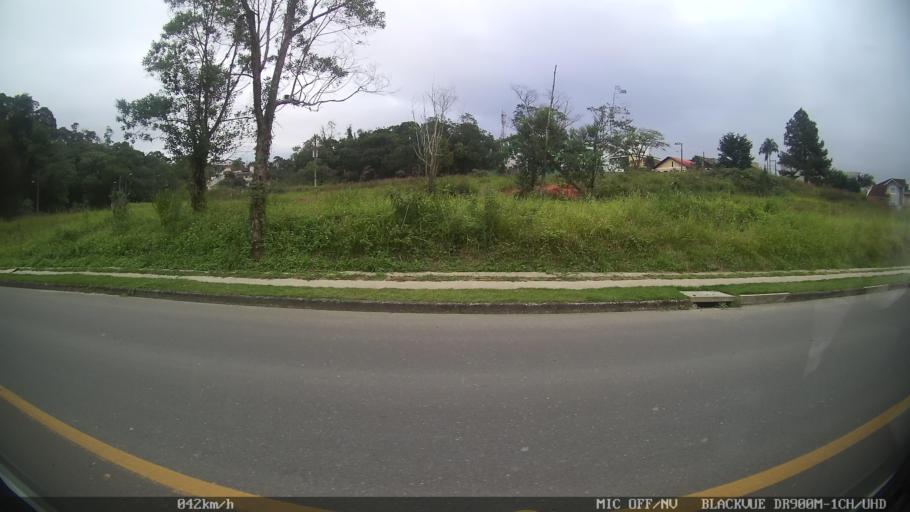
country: BR
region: Santa Catarina
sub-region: Joinville
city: Joinville
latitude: -26.2789
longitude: -48.8784
